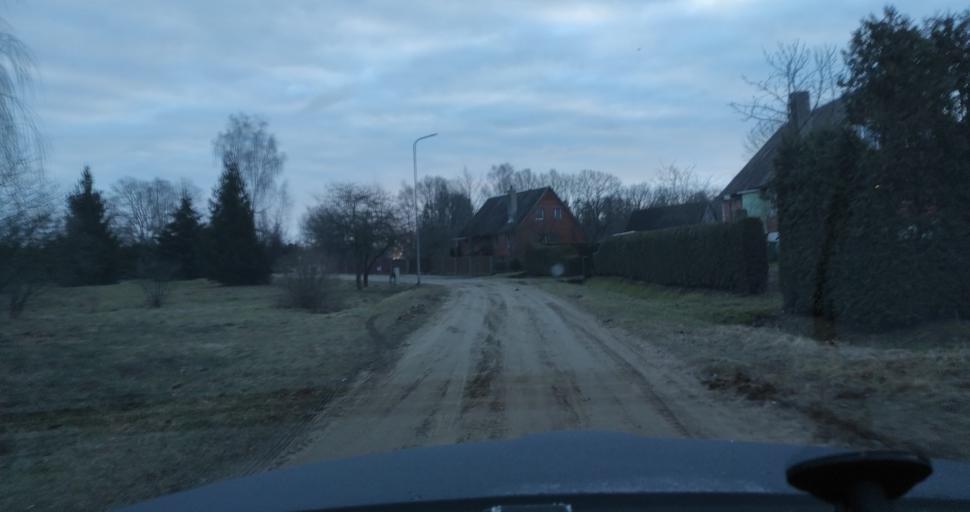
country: LV
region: Aizpute
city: Aizpute
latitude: 56.8331
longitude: 21.7692
